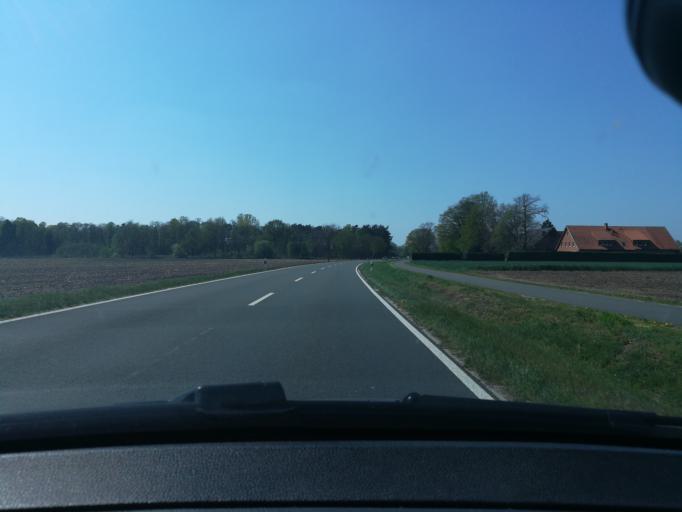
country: DE
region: North Rhine-Westphalia
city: Versmold
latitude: 52.0057
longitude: 8.1934
